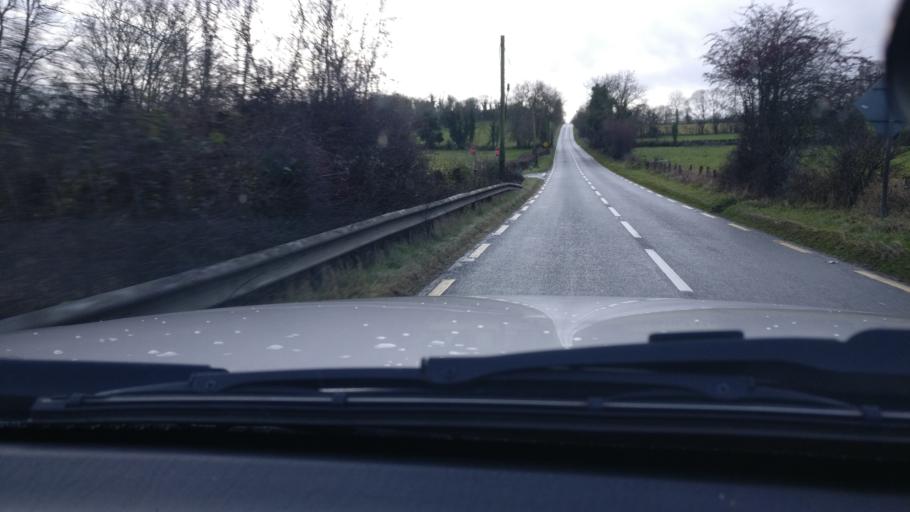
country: IE
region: Leinster
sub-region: An Iarmhi
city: Moate
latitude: 53.6224
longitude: -7.6989
